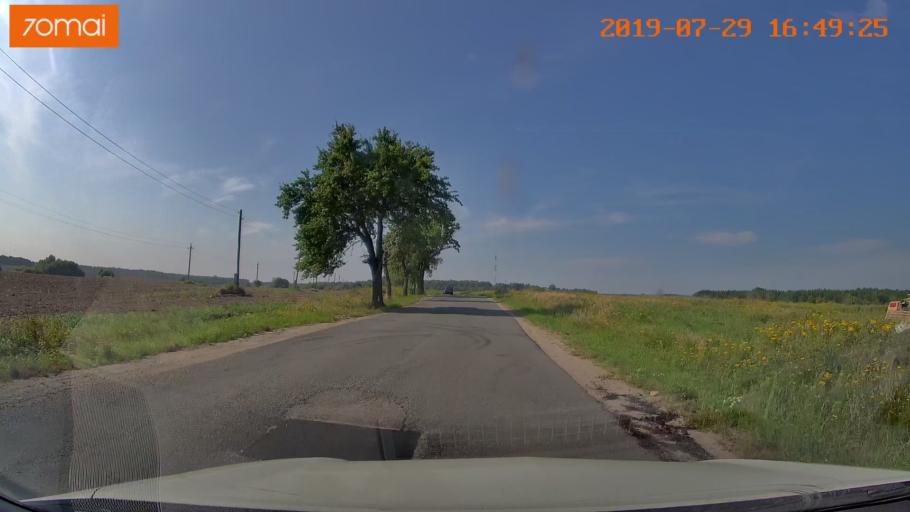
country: RU
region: Kaliningrad
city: Primorsk
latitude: 54.7939
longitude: 20.0656
